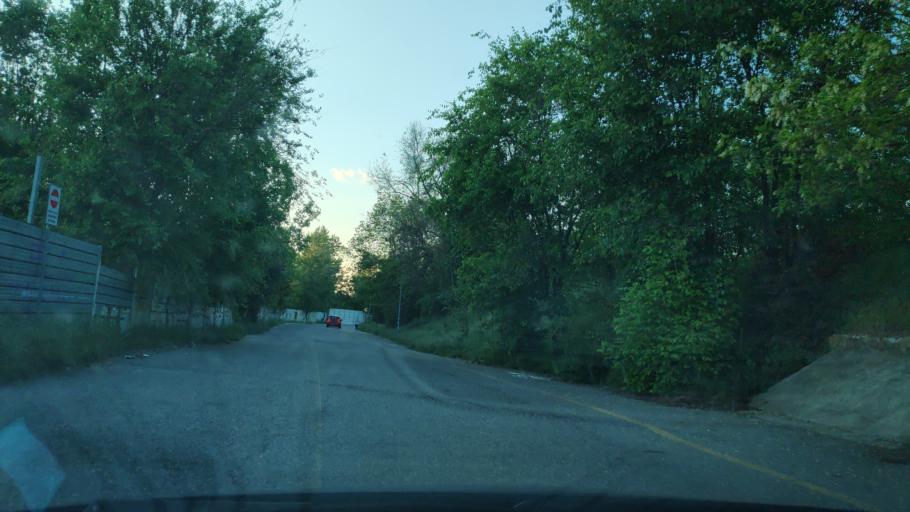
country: IT
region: Lombardy
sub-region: Citta metropolitana di Milano
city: Segrate
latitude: 45.4817
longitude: 9.2997
